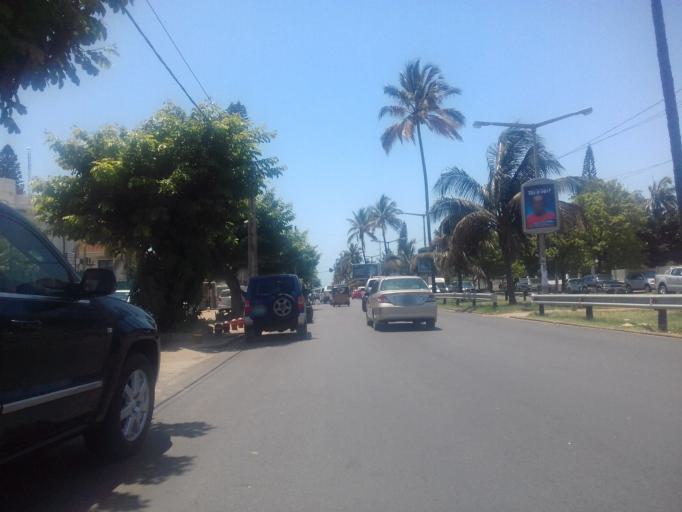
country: MZ
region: Maputo City
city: Maputo
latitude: -25.9571
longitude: 32.5967
